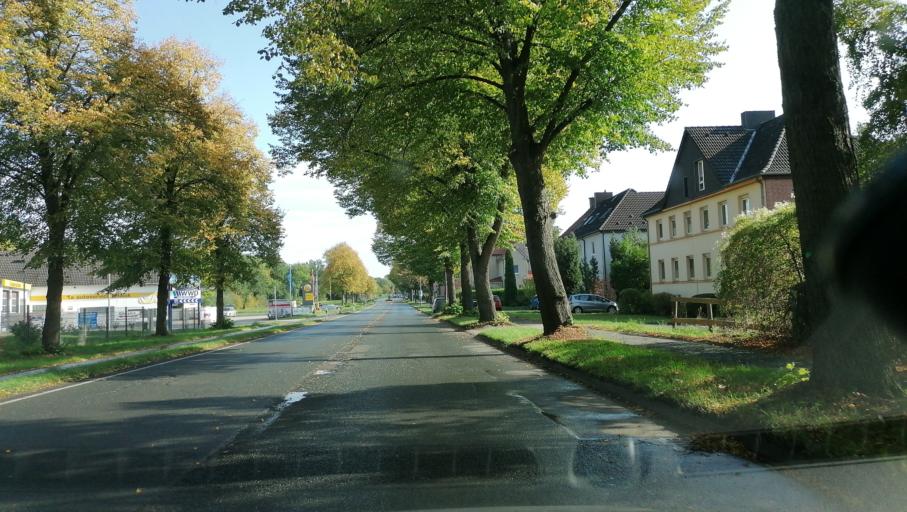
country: DE
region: North Rhine-Westphalia
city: Waltrop
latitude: 51.6227
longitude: 7.4212
